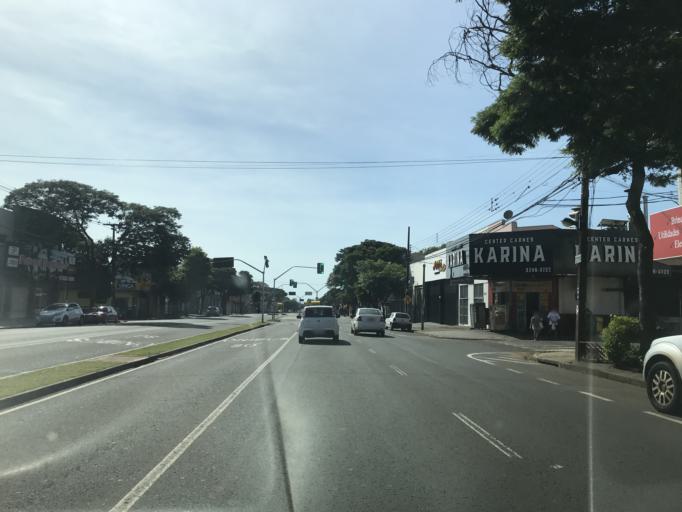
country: BR
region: Parana
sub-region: Maringa
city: Maringa
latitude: -23.4087
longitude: -51.9308
